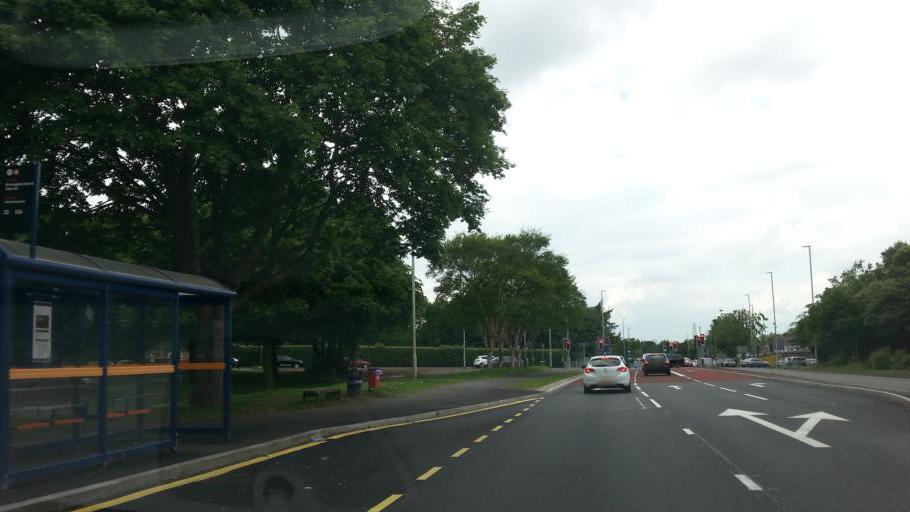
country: GB
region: England
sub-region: Sandwell
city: Tipton
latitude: 52.5471
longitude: -2.0938
